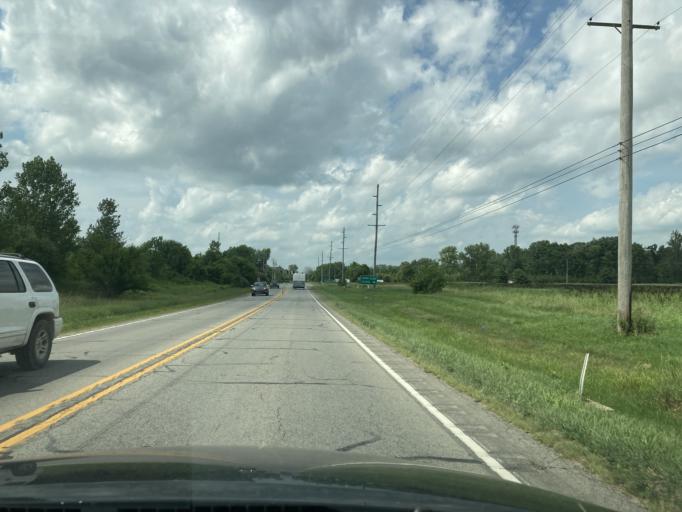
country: US
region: Indiana
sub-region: Boone County
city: Zionsville
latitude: 39.9958
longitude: -86.2633
